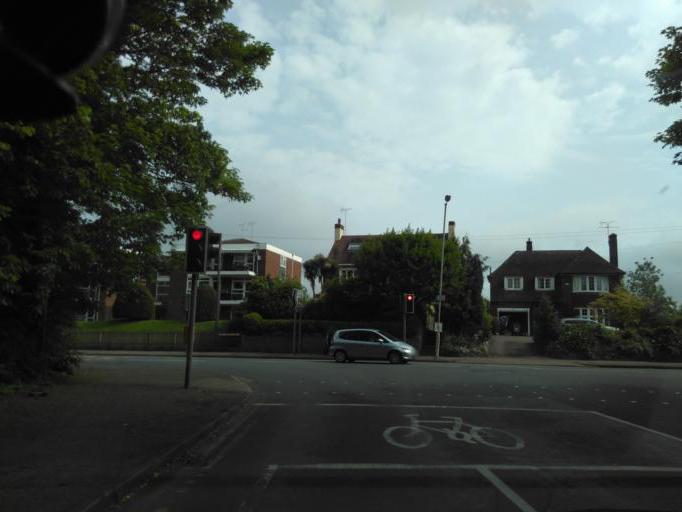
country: GB
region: England
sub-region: Kent
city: Canterbury
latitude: 51.2676
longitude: 1.0938
